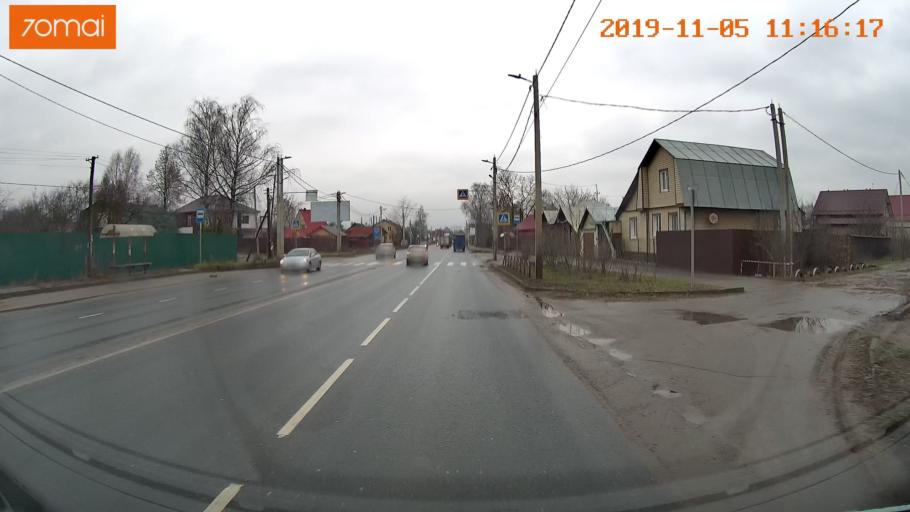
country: RU
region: Ivanovo
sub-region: Gorod Ivanovo
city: Ivanovo
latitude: 56.9835
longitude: 40.9535
